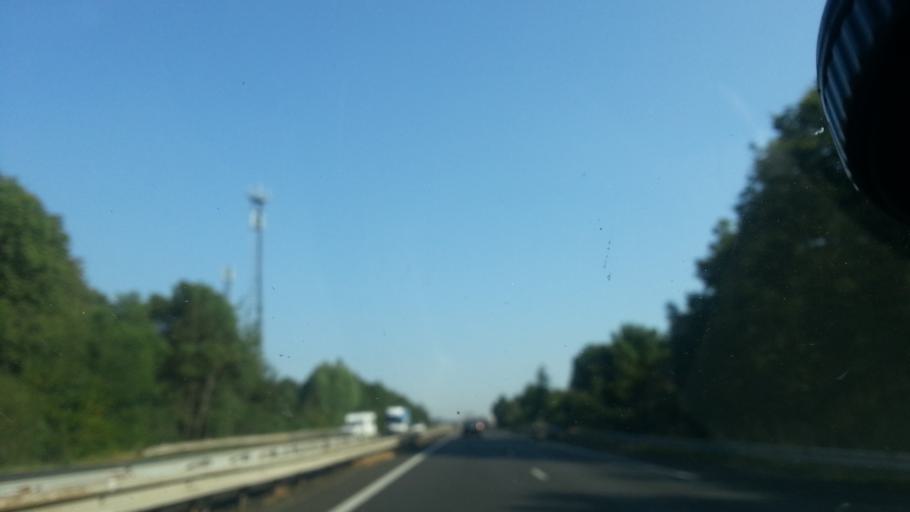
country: FR
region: Poitou-Charentes
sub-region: Departement de la Vienne
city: Les Ormes
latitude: 46.9644
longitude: 0.5484
